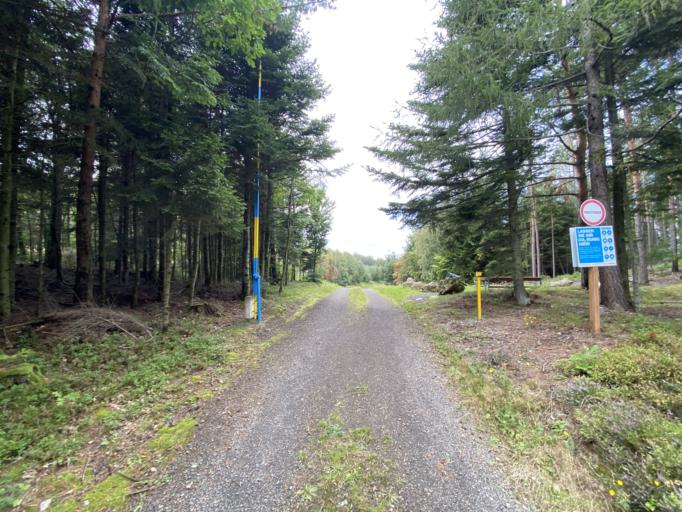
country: AT
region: Burgenland
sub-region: Politischer Bezirk Oberpullendorf
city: Weingraben
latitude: 47.5658
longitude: 16.3390
